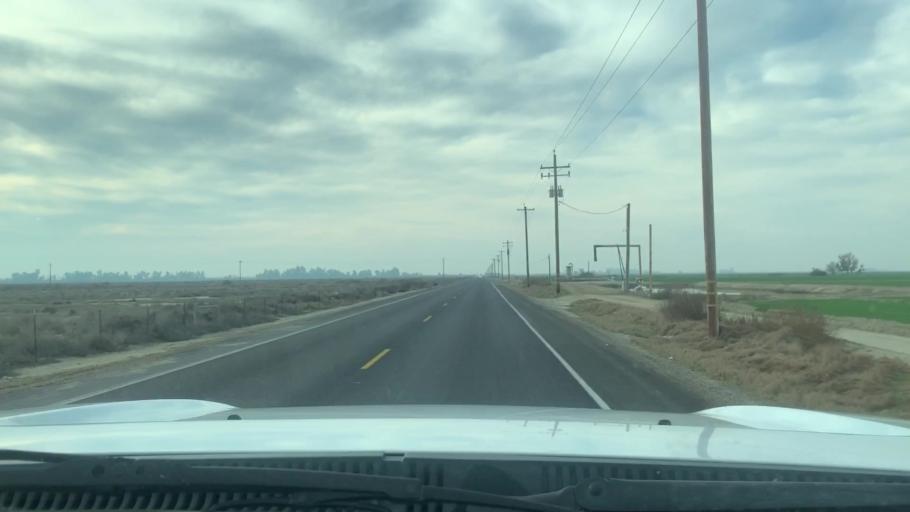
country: US
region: California
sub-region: Kern County
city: Buttonwillow
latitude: 35.4421
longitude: -119.3800
